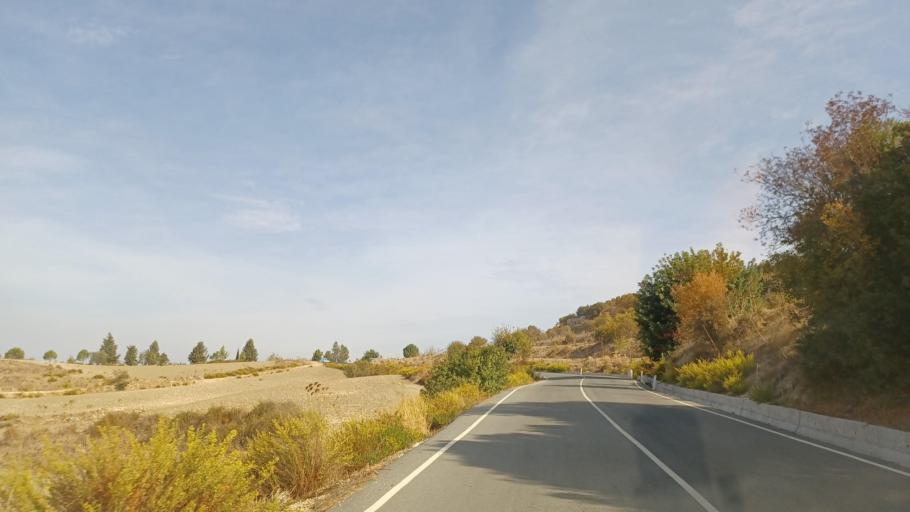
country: CY
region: Pafos
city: Polis
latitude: 34.9831
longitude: 32.5001
